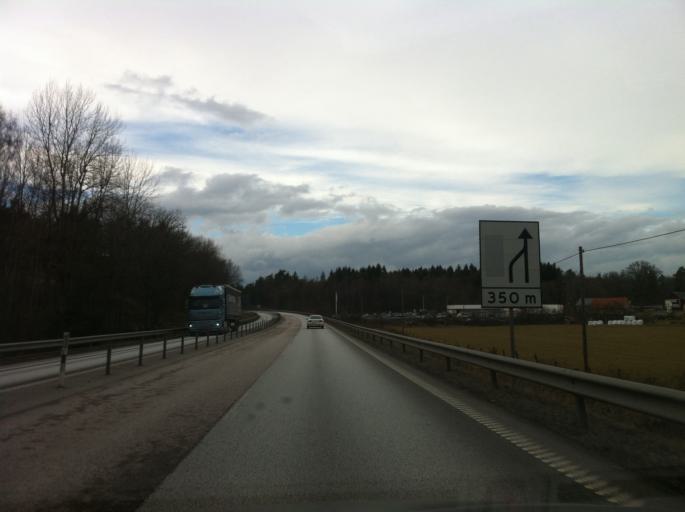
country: SE
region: Blekinge
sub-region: Karlshamns Kommun
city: Karlshamn
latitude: 56.1962
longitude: 14.9710
